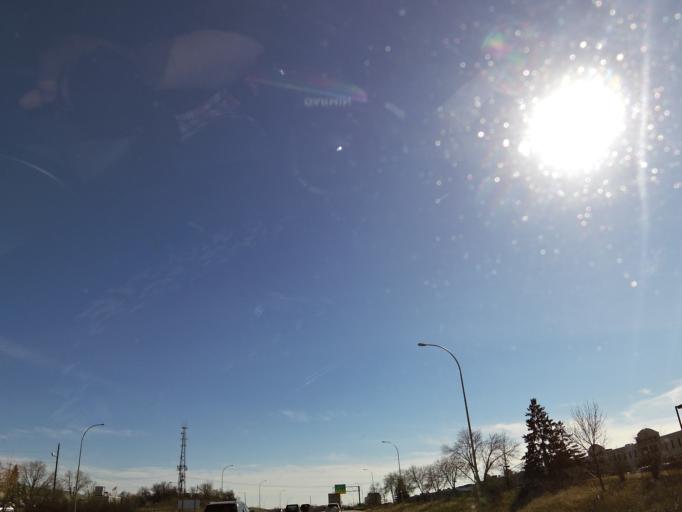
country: US
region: Minnesota
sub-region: Hennepin County
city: Edina
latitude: 44.8706
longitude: -93.3969
